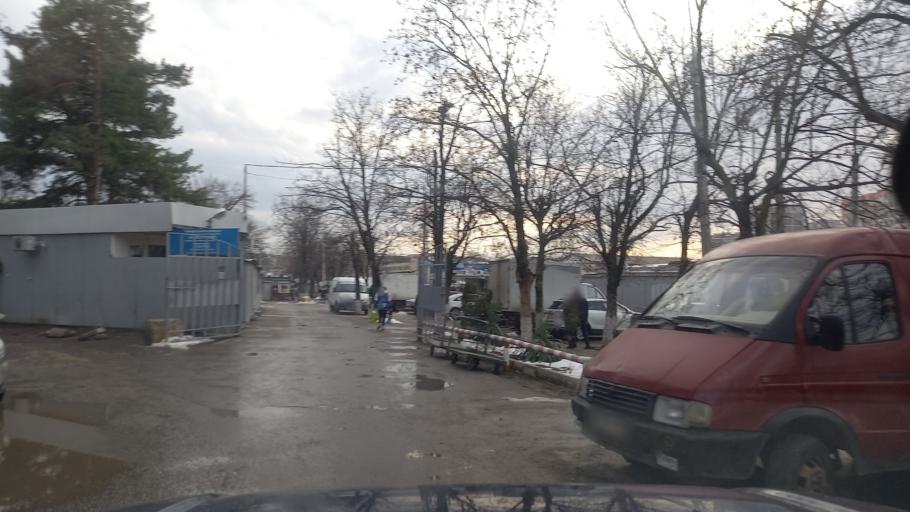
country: RU
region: Krasnodarskiy
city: Pashkovskiy
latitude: 45.0206
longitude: 39.0432
